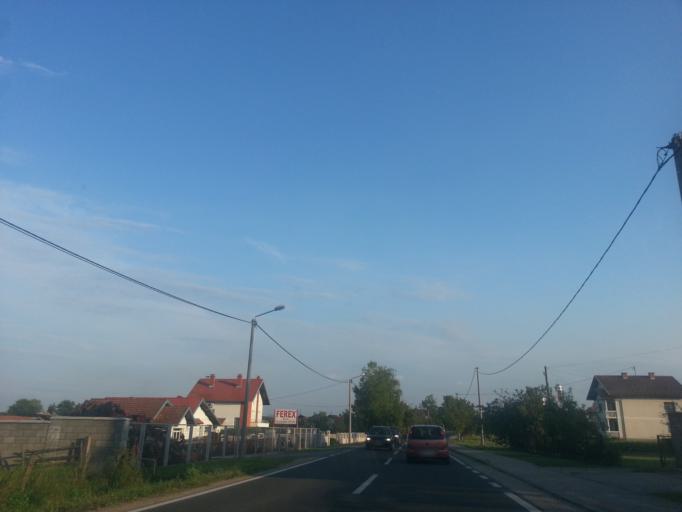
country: BA
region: Brcko
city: Brcko
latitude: 44.8359
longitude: 18.8202
